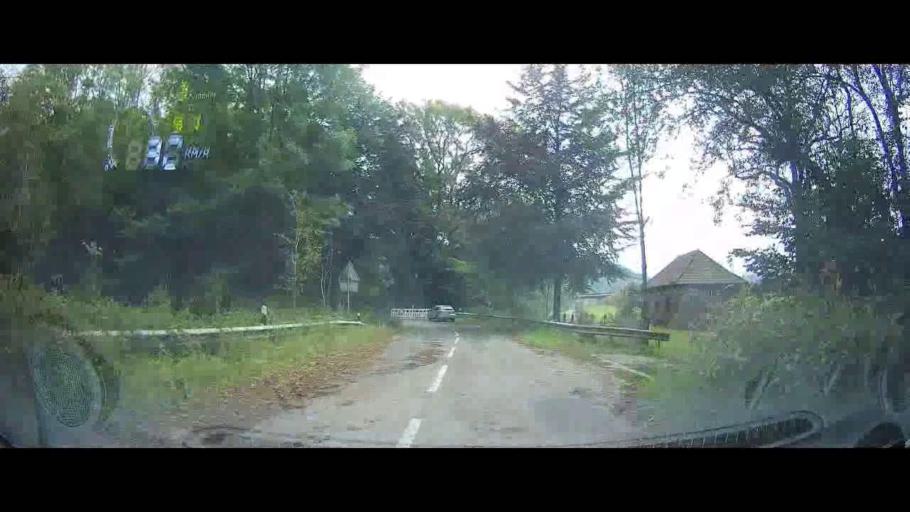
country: DE
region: Lower Saxony
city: Hardegsen
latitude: 51.6591
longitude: 9.7617
